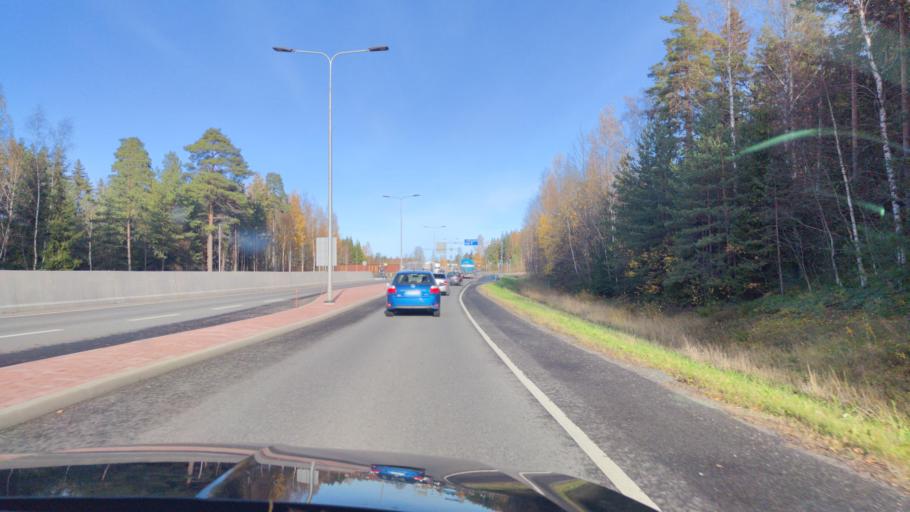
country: FI
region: Varsinais-Suomi
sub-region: Turku
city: Kaarina
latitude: 60.4267
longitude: 22.3813
